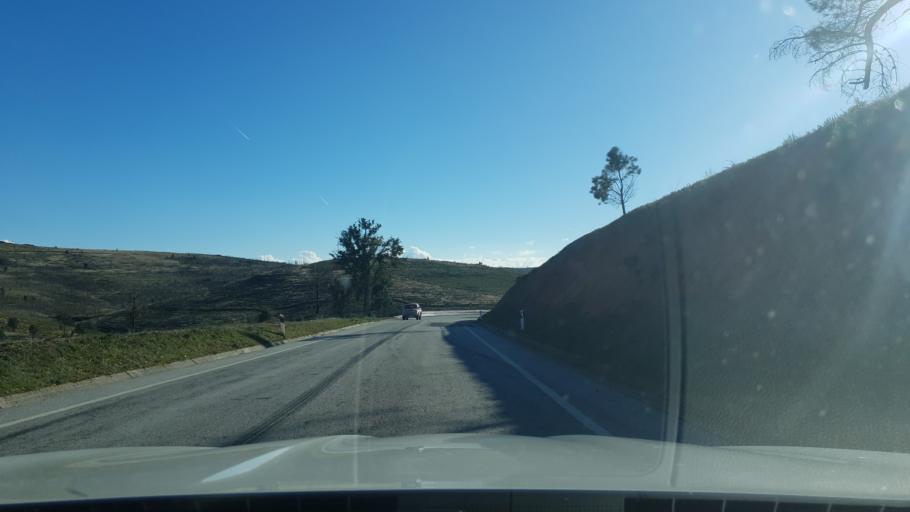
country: PT
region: Braganca
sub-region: Freixo de Espada A Cinta
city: Freixo de Espada a Cinta
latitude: 41.1708
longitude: -6.7918
